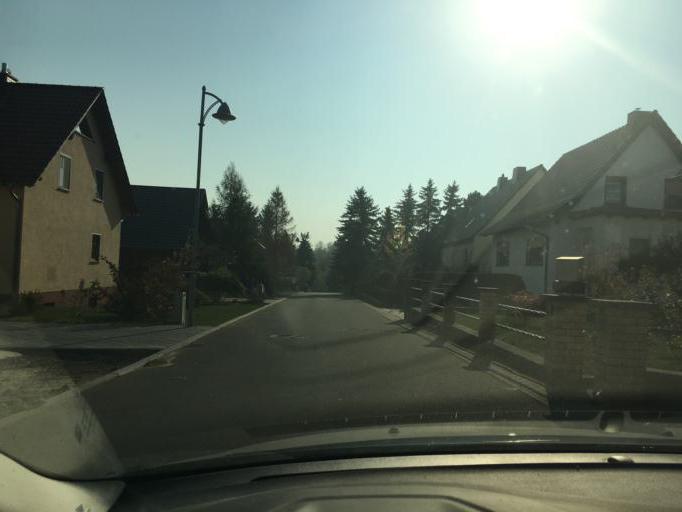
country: DE
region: Saxony
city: Wermsdorf
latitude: 51.2812
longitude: 12.9307
